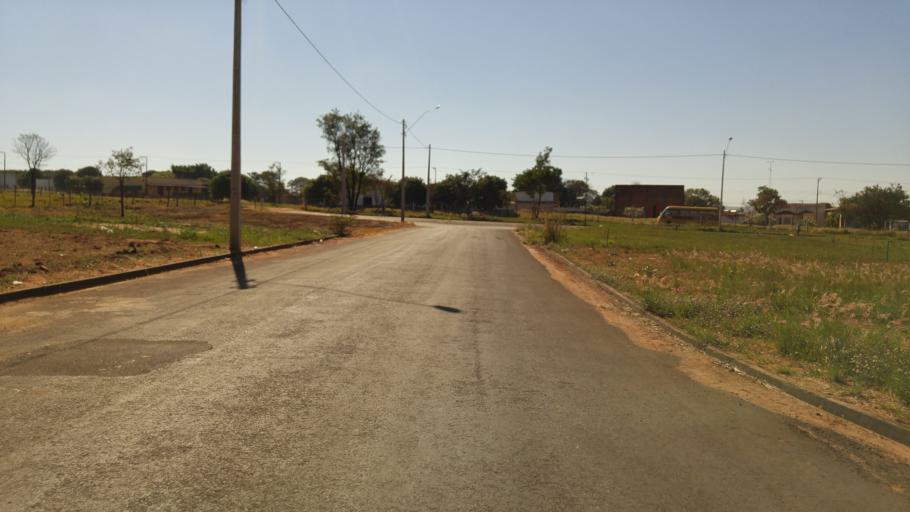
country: BR
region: Sao Paulo
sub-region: Paraguacu Paulista
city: Paraguacu Paulista
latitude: -22.4387
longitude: -50.5868
